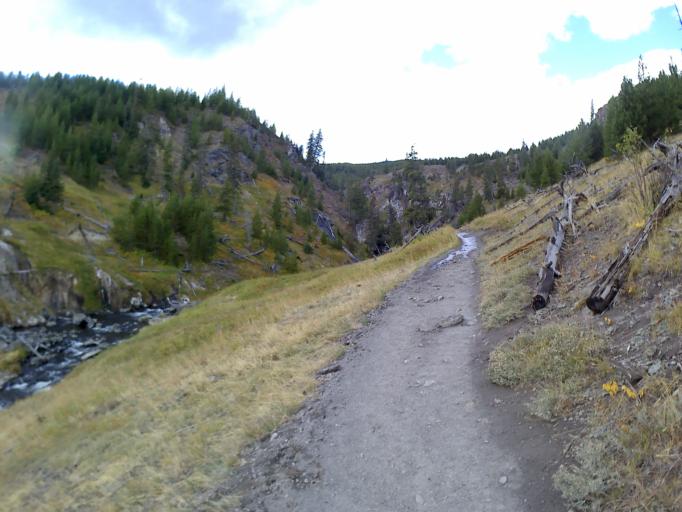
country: US
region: Montana
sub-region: Gallatin County
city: West Yellowstone
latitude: 44.4837
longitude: -110.8706
